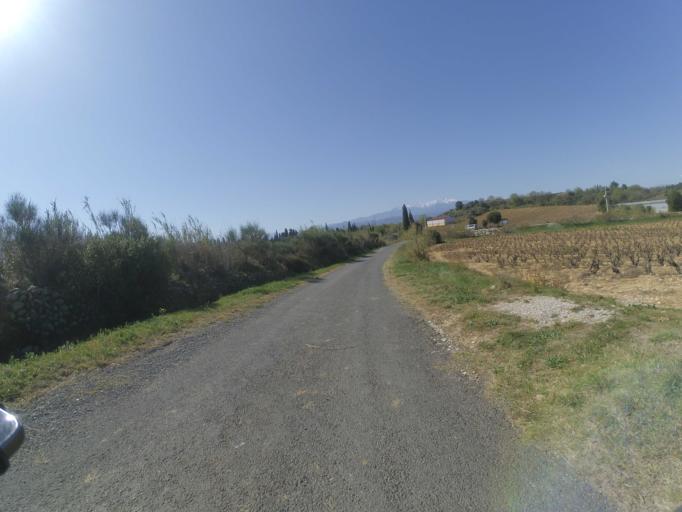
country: FR
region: Languedoc-Roussillon
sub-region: Departement des Pyrenees-Orientales
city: Pezilla-la-Riviere
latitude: 42.7067
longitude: 2.7750
